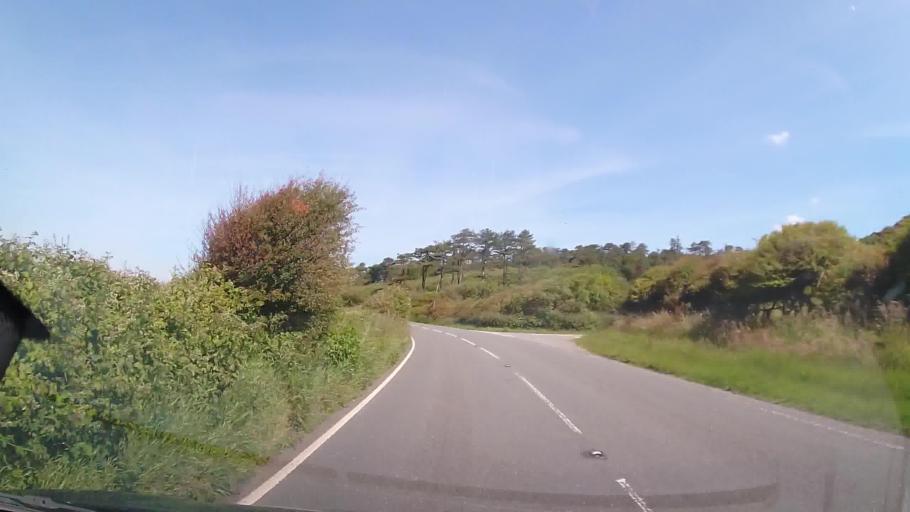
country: GB
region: Wales
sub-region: Gwynedd
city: Tywyn
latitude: 52.5599
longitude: -4.0712
